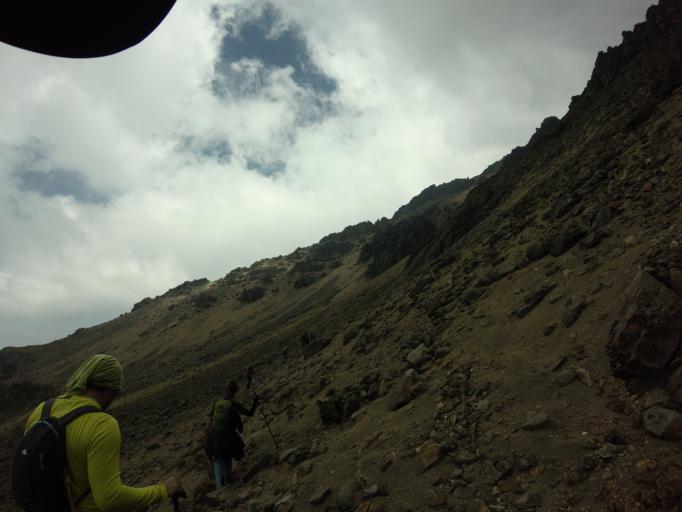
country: MX
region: Mexico
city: Amecameca de Juarez
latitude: 19.1500
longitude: -98.6381
